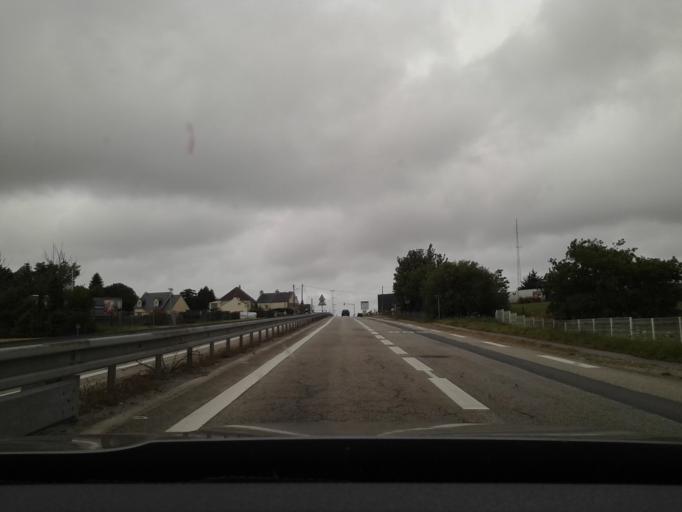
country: FR
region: Lower Normandy
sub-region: Departement de la Manche
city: La Glacerie
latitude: 49.6062
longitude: -1.5992
